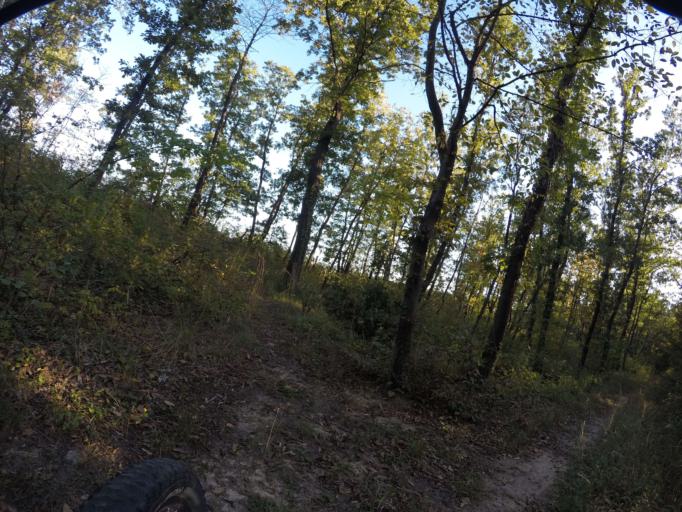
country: AT
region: Lower Austria
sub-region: Politischer Bezirk Bruck an der Leitha
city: Mannersdorf am Leithagebirge
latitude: 47.9633
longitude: 16.6021
